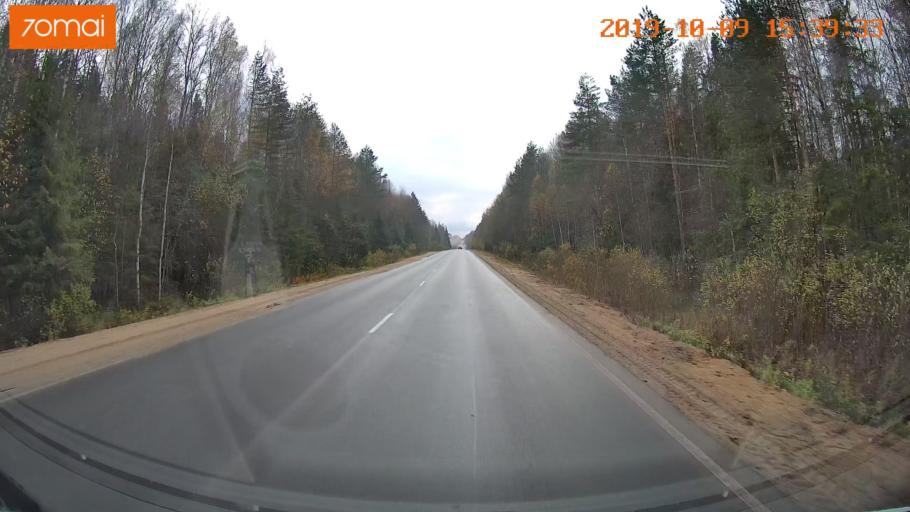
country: RU
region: Kostroma
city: Oktyabr'skiy
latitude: 57.8960
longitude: 41.1623
